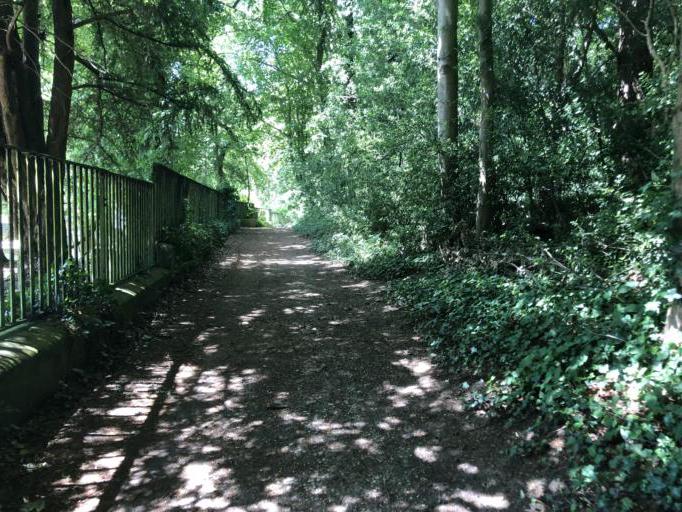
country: GB
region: England
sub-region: Greater London
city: Wandsworth
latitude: 51.4408
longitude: -0.2385
